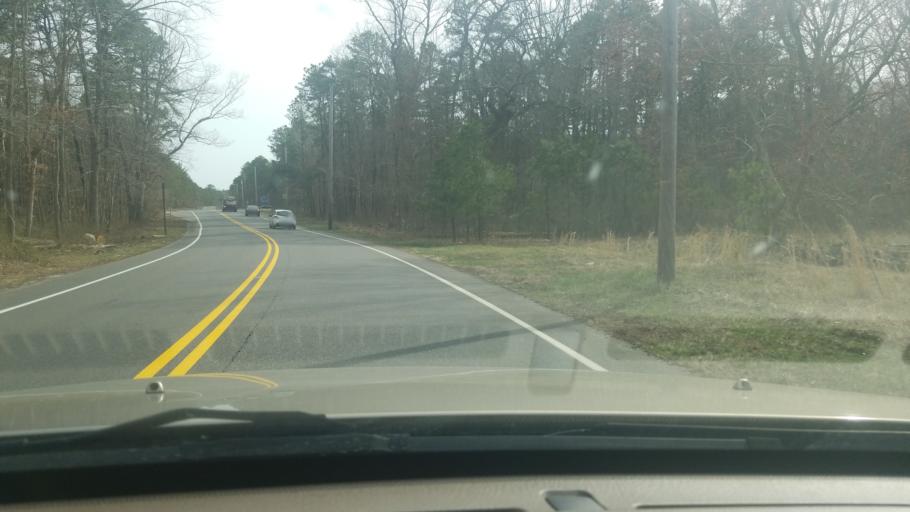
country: US
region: New Jersey
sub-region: Ocean County
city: Vista Center
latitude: 40.1710
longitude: -74.3498
